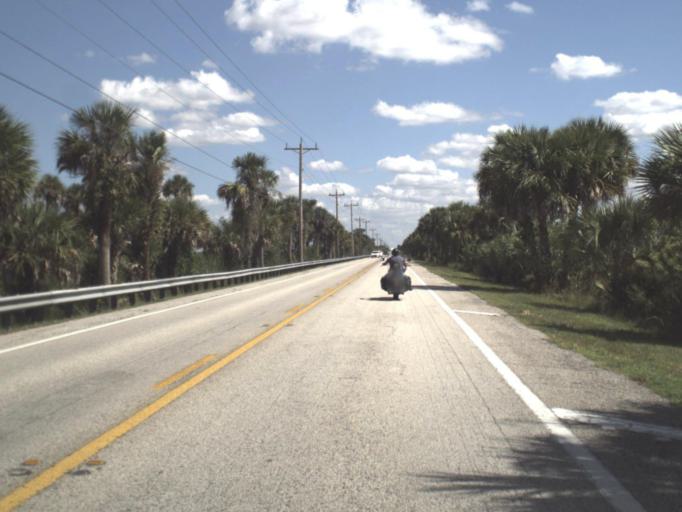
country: US
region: Florida
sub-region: Collier County
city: Marco
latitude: 25.9306
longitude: -81.4394
